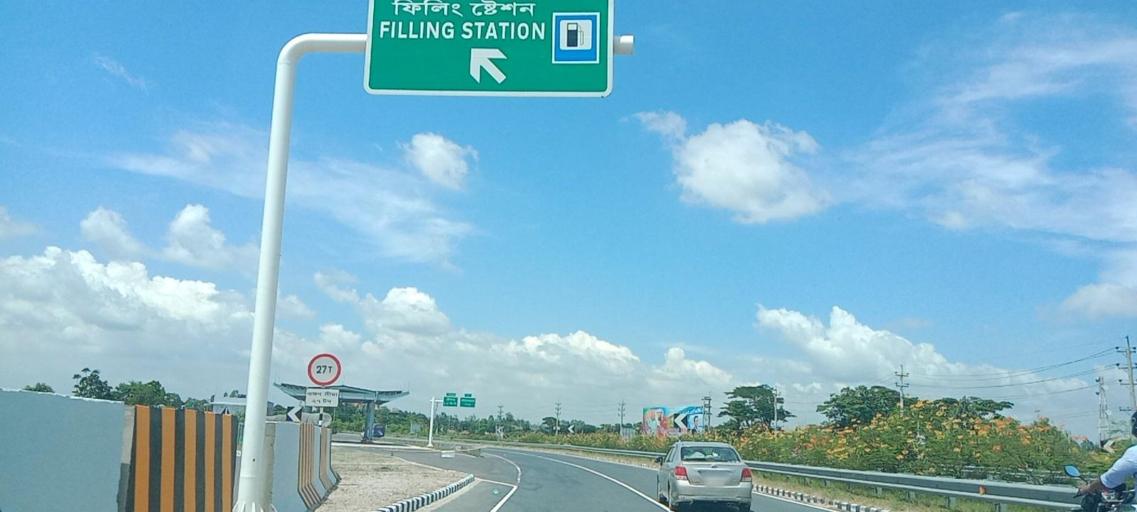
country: BD
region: Dhaka
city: Dohar
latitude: 23.5278
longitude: 90.2885
